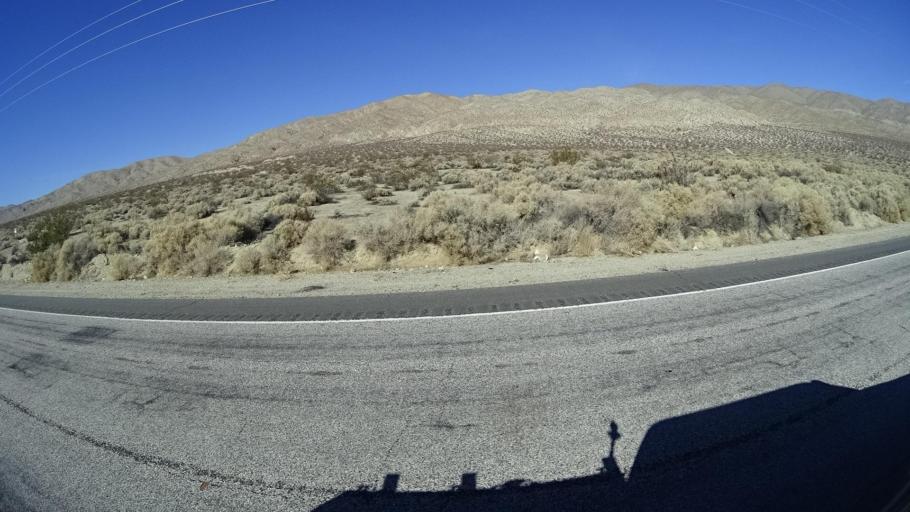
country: US
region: California
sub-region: Kern County
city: California City
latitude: 35.3692
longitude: -117.8825
